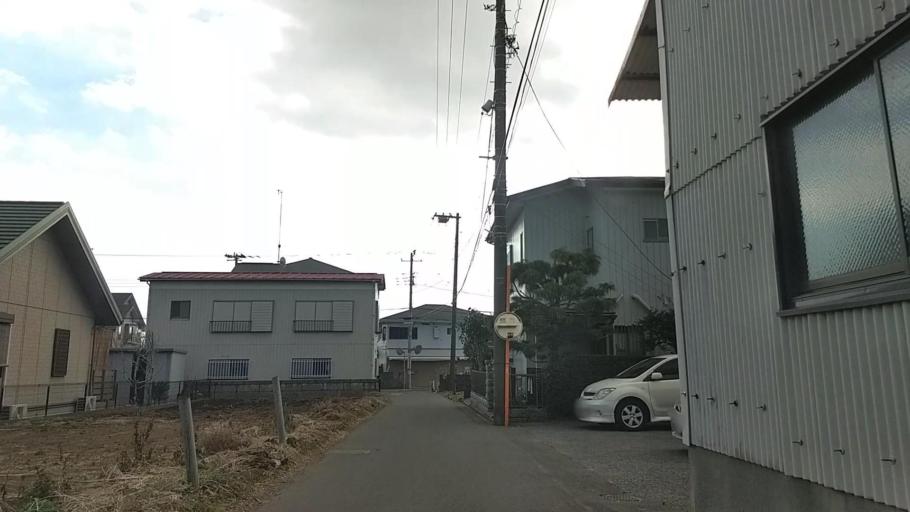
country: JP
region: Kanagawa
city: Isehara
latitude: 35.4063
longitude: 139.3107
